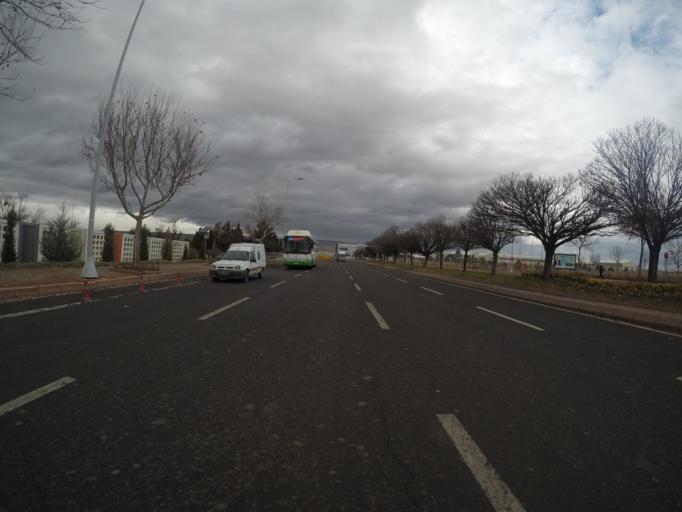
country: TR
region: Kayseri
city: Kayseri
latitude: 38.7626
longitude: 35.4817
